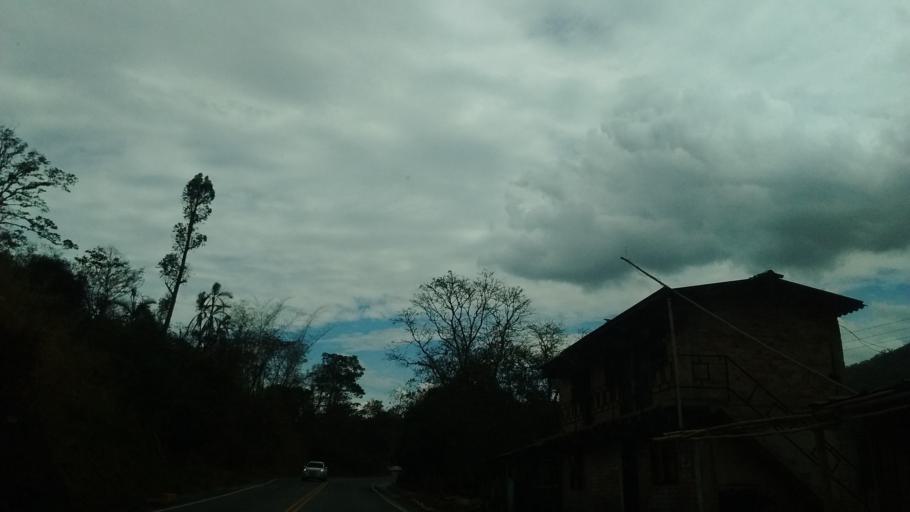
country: CO
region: Cauca
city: Rosas
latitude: 2.2780
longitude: -76.7098
